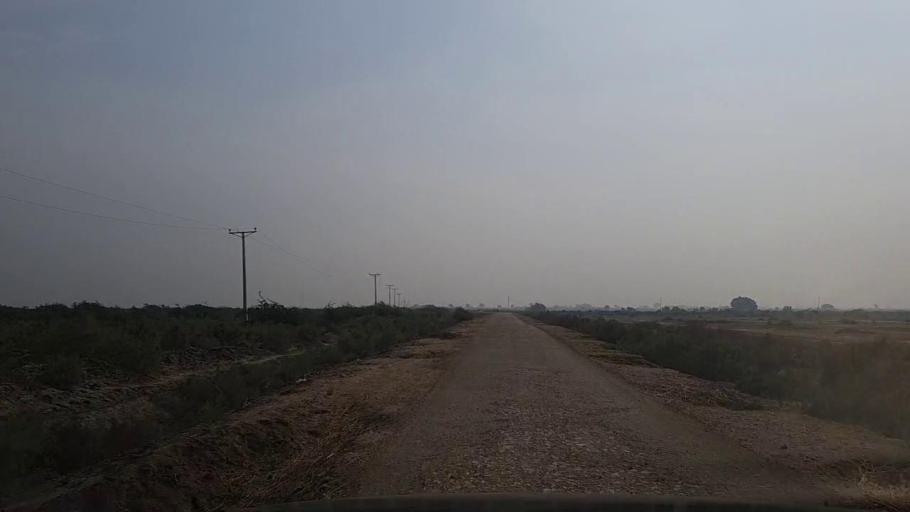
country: PK
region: Sindh
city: Mirpur Sakro
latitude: 24.3875
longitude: 67.7525
